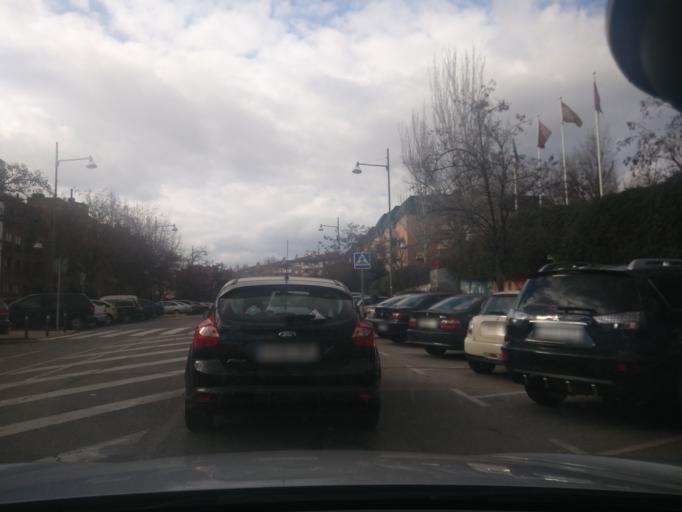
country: ES
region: Madrid
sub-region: Provincia de Madrid
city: Alcobendas
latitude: 40.5455
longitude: -3.6447
